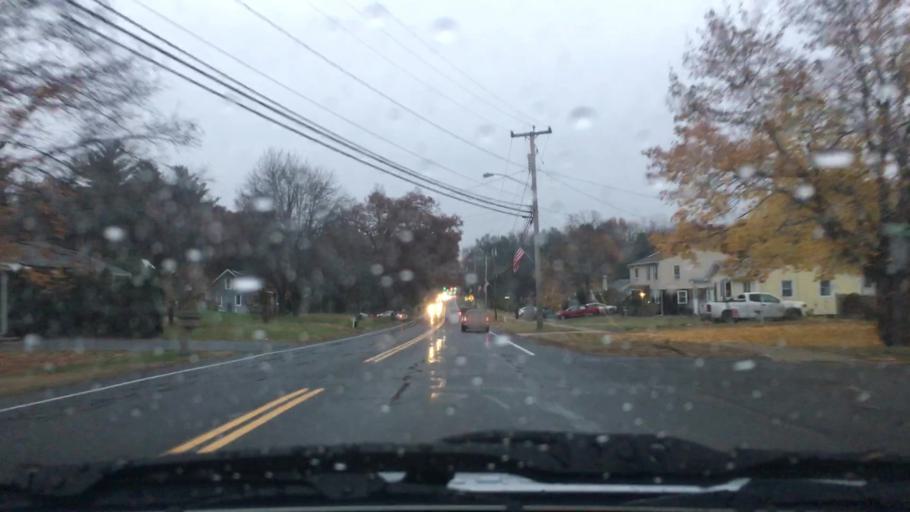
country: US
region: Massachusetts
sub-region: Hampden County
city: Southwick
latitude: 42.0623
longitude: -72.7619
